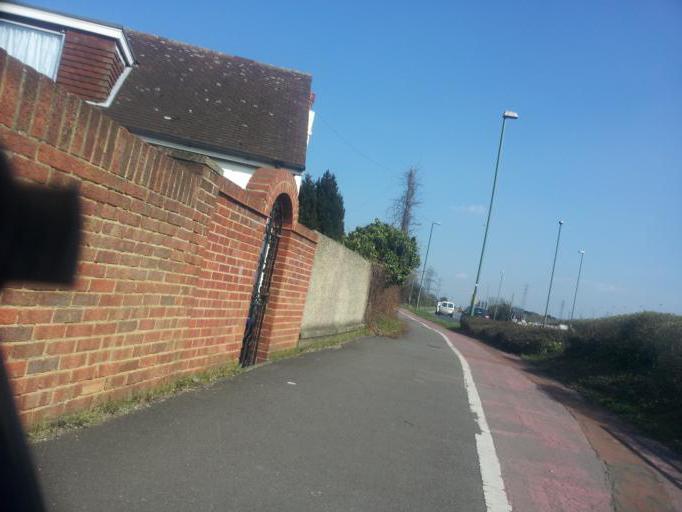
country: GB
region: England
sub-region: Kent
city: Stone
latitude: 51.4384
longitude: 0.2544
